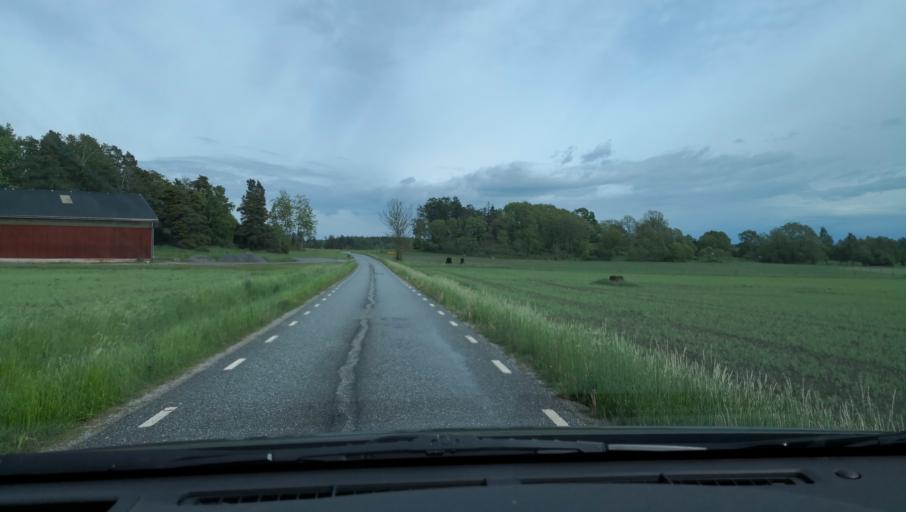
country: SE
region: Uppsala
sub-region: Enkopings Kommun
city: Orsundsbro
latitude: 59.7051
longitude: 17.4054
